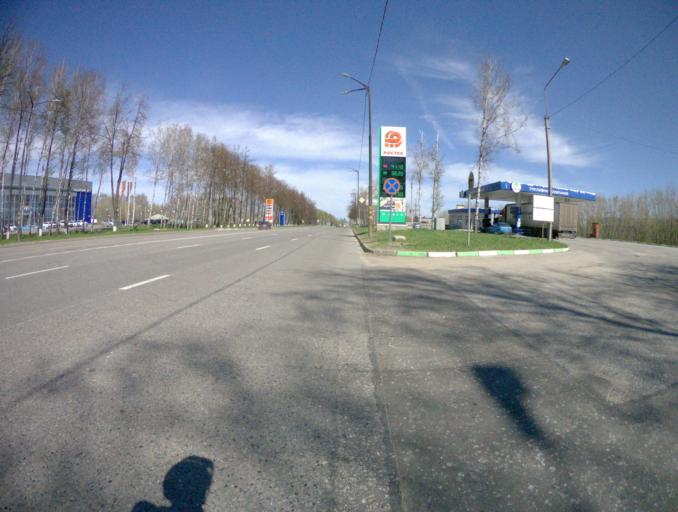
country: RU
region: Vladimir
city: Bogolyubovo
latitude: 56.1741
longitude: 40.4957
